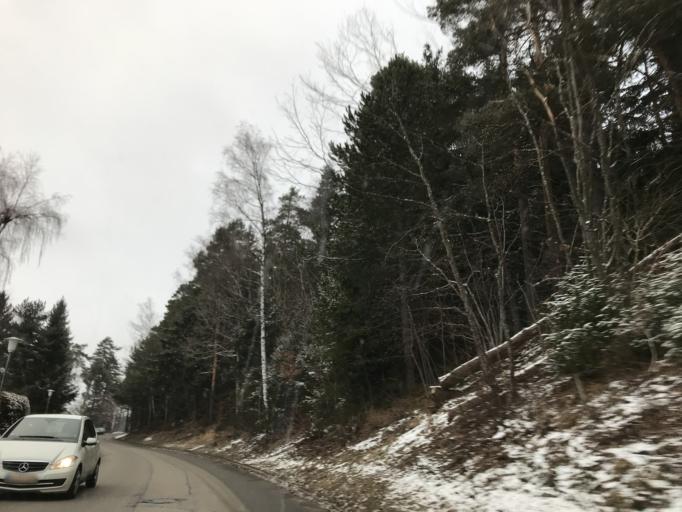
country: DE
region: Baden-Wuerttemberg
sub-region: Freiburg Region
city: Sankt Georgen im Schwarzwald
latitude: 48.1303
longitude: 8.3419
